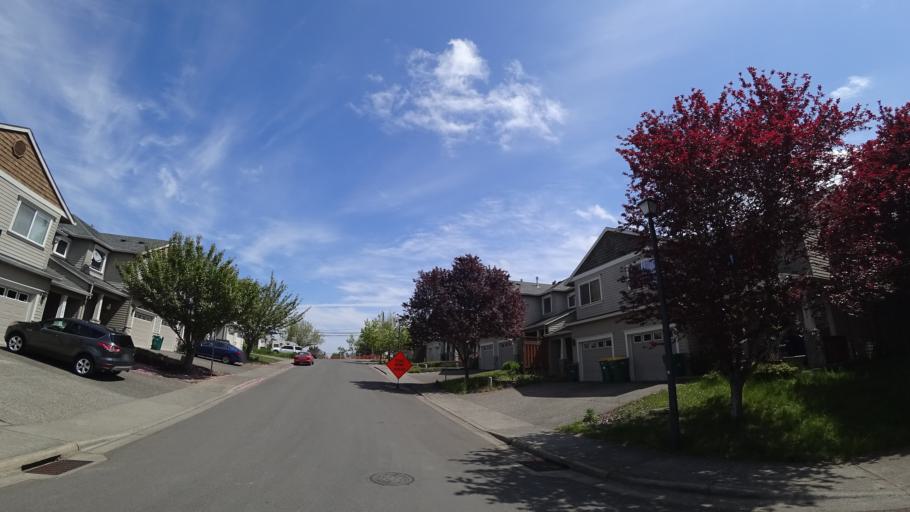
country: US
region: Oregon
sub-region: Washington County
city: Aloha
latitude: 45.4676
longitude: -122.8850
